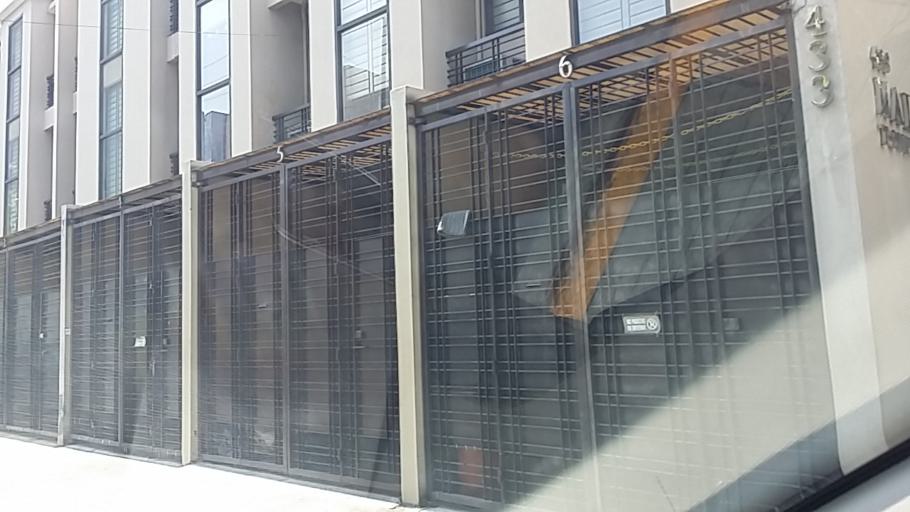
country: PH
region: Metro Manila
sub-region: Mandaluyong
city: Mandaluyong City
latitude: 14.5768
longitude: 121.0374
